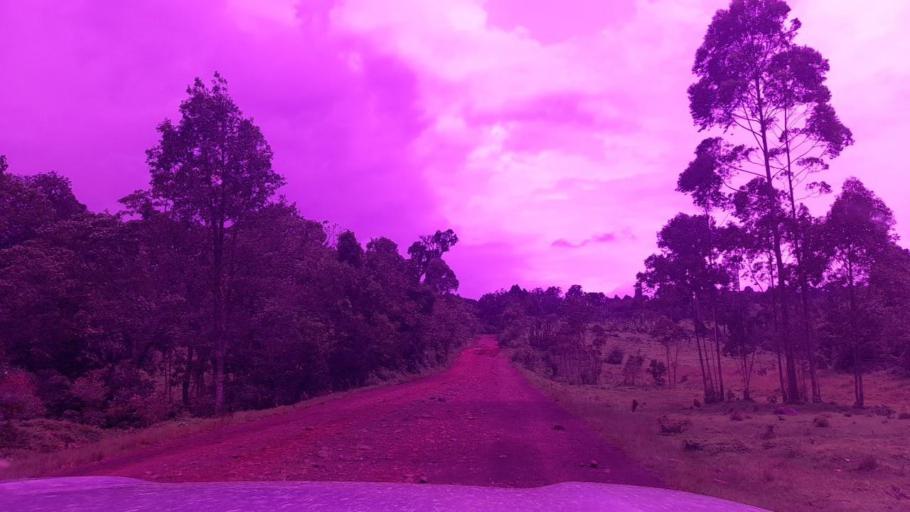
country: ET
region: Southern Nations, Nationalities, and People's Region
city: Tippi
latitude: 7.6302
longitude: 35.5627
